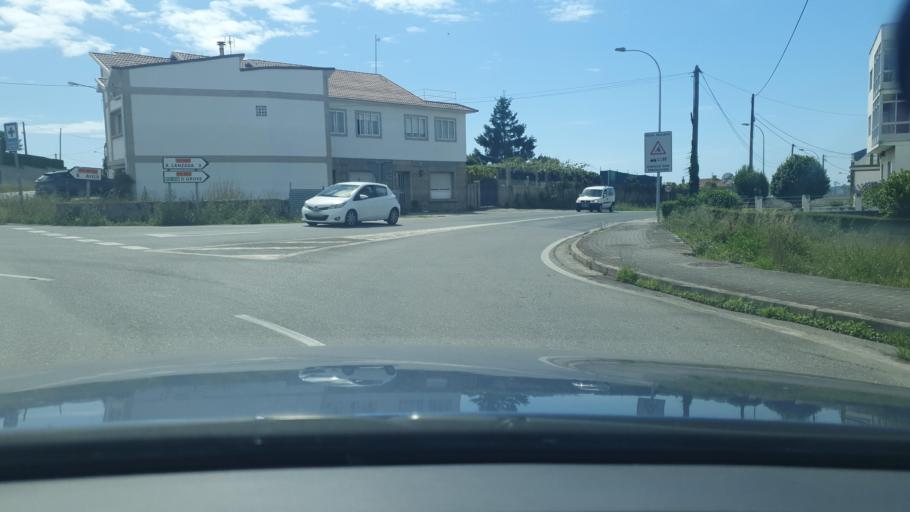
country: ES
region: Galicia
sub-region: Provincia de Pontevedra
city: O Grove
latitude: 42.4400
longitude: -8.8483
